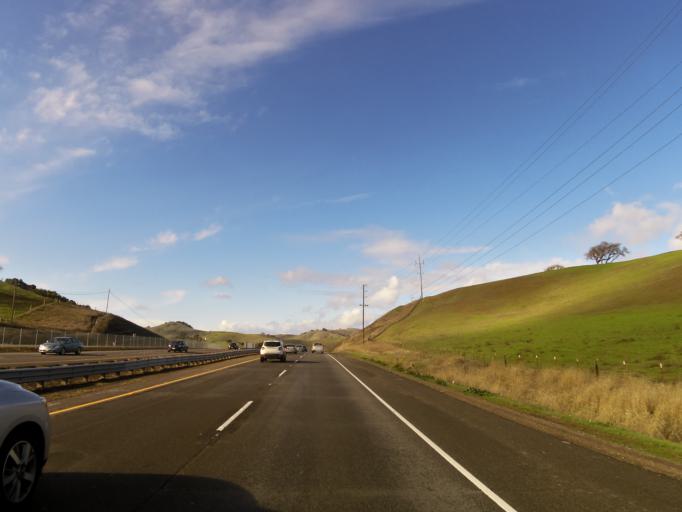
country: US
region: California
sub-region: Marin County
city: Novato
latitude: 38.1753
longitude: -122.5923
